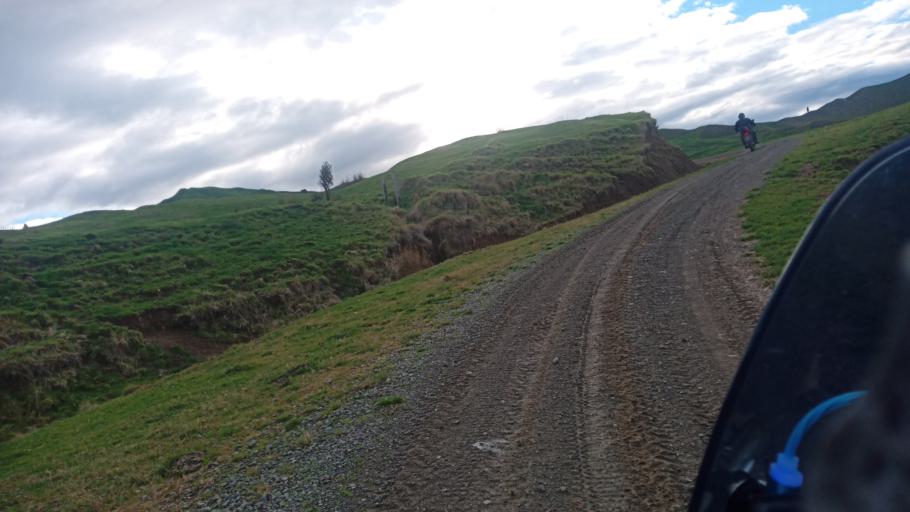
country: NZ
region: Gisborne
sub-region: Gisborne District
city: Gisborne
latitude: -38.3478
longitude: 177.9301
